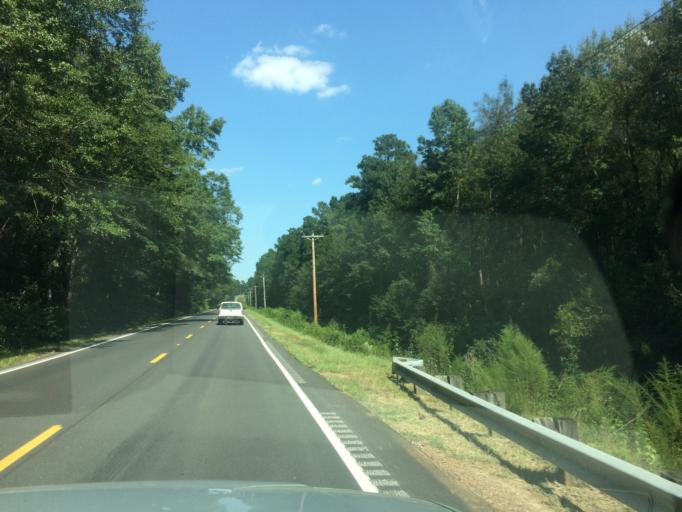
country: US
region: South Carolina
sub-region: Barnwell County
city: Williston
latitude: 33.5771
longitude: -81.5161
